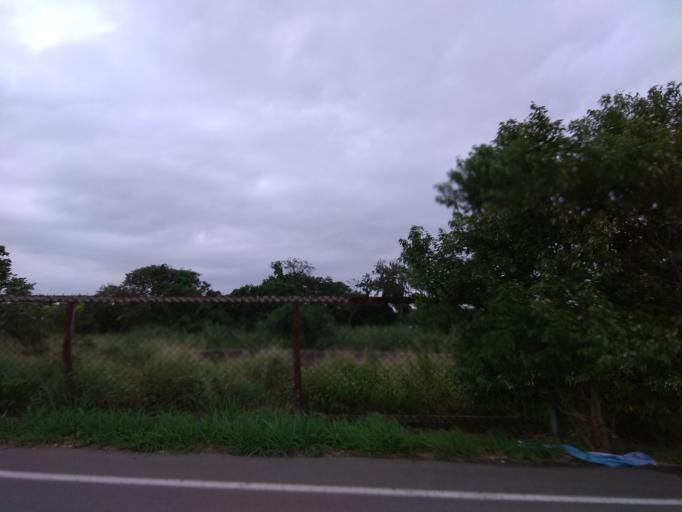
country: TW
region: Taiwan
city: Taoyuan City
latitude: 25.0523
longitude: 121.2140
